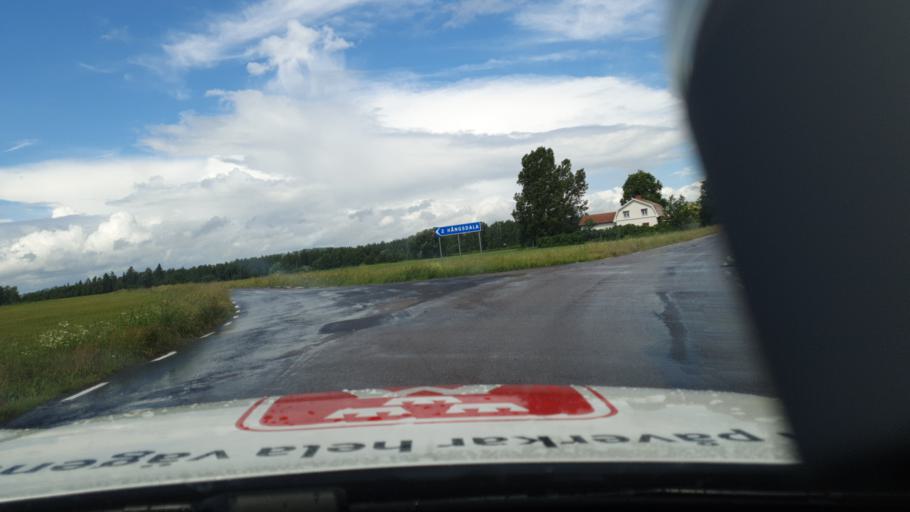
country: SE
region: Vaestra Goetaland
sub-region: Tidaholms Kommun
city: Tidaholm
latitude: 58.1003
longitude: 13.7958
